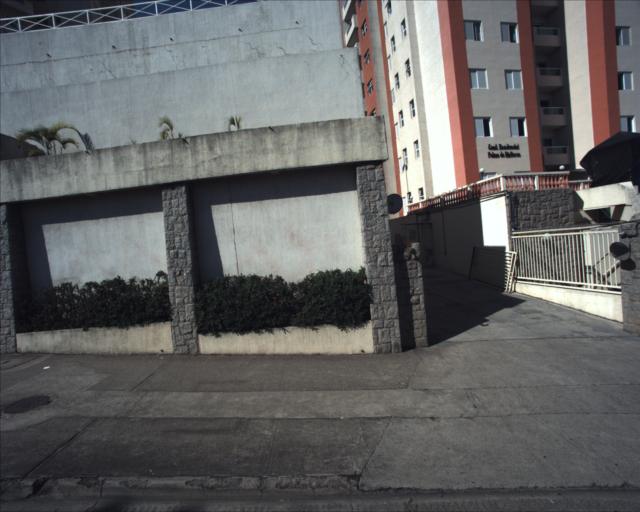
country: BR
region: Sao Paulo
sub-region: Sorocaba
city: Sorocaba
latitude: -23.4911
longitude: -47.4320
